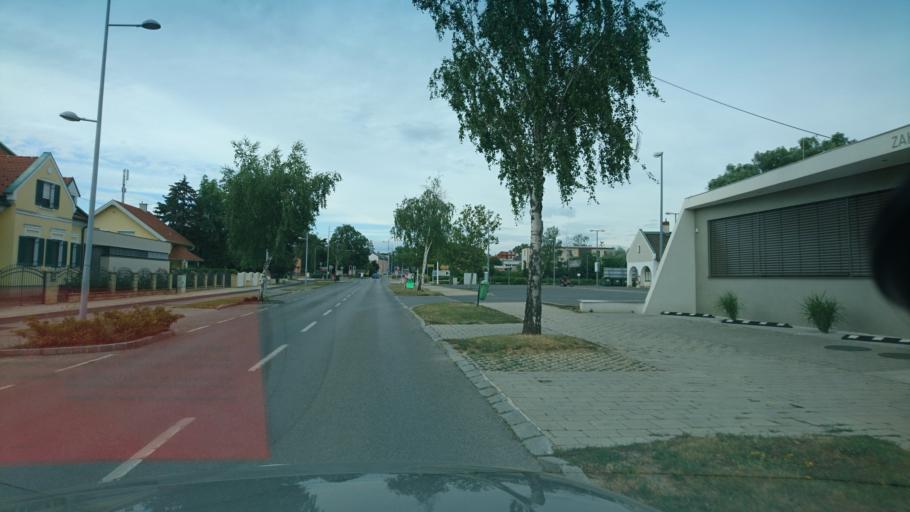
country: AT
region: Burgenland
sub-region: Politischer Bezirk Neusiedl am See
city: Neusiedl am See
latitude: 47.9412
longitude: 16.8460
